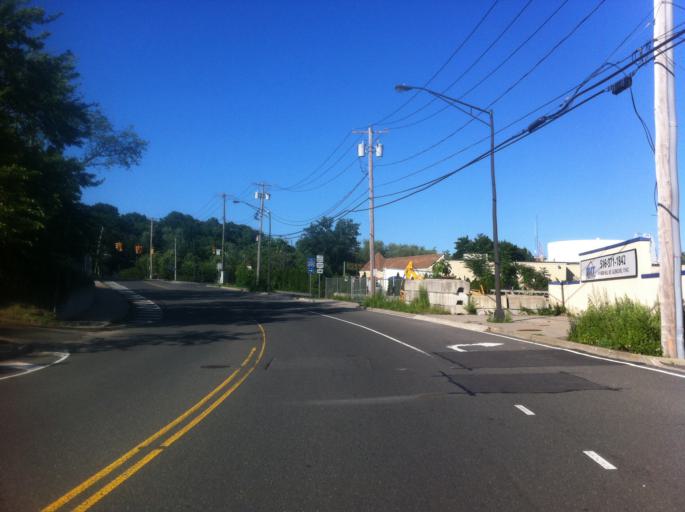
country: US
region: New York
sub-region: Nassau County
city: Glen Cove
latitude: 40.8611
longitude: -73.6402
